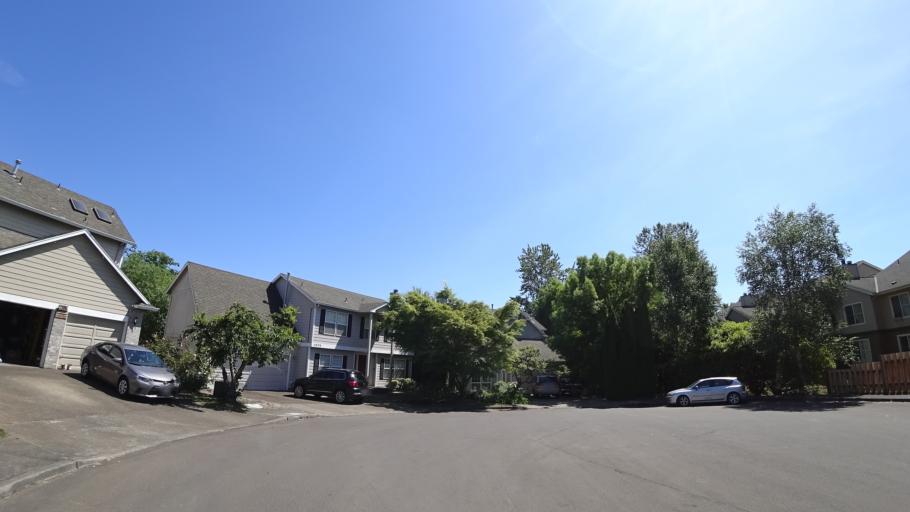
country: US
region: Oregon
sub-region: Washington County
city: King City
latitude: 45.4400
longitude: -122.8125
